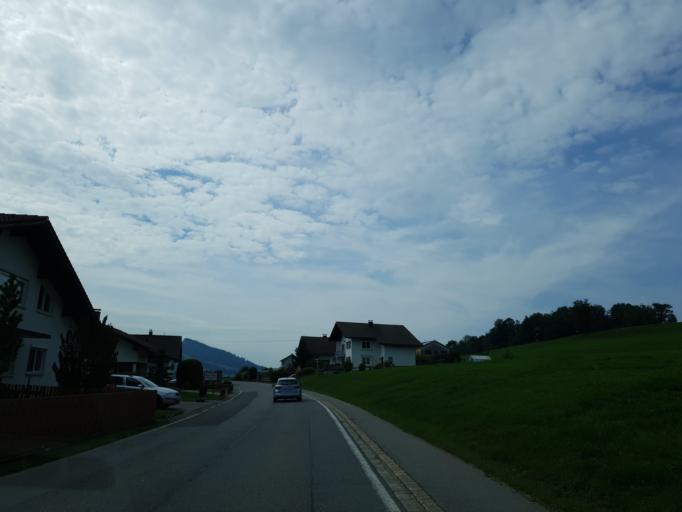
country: AT
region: Vorarlberg
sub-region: Politischer Bezirk Bregenz
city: Doren
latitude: 47.4885
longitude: 9.8628
